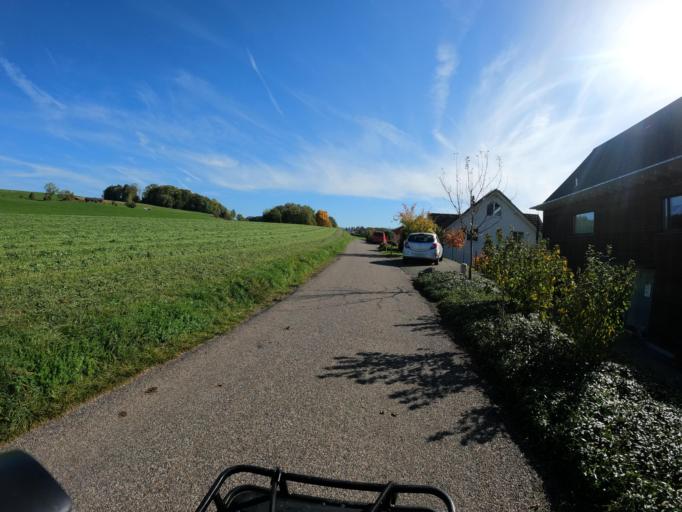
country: CH
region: Zurich
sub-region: Bezirk Affoltern
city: Mettmenstetten
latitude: 47.2422
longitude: 8.4710
